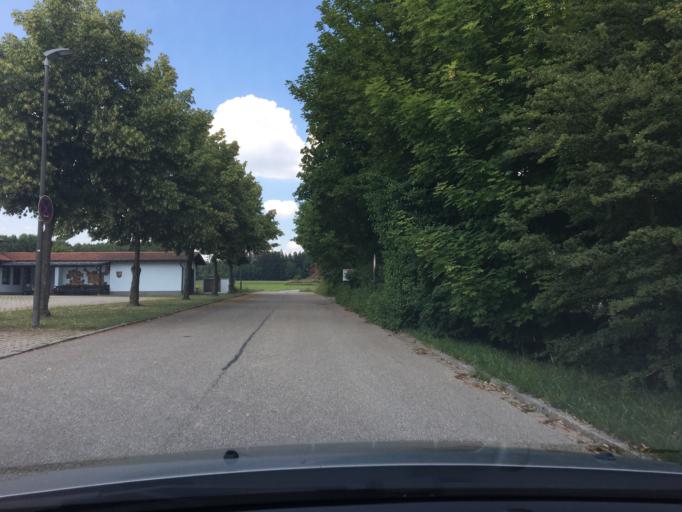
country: DE
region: Bavaria
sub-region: Upper Bavaria
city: Neumarkt-Sankt Veit
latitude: 48.3688
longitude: 12.5116
